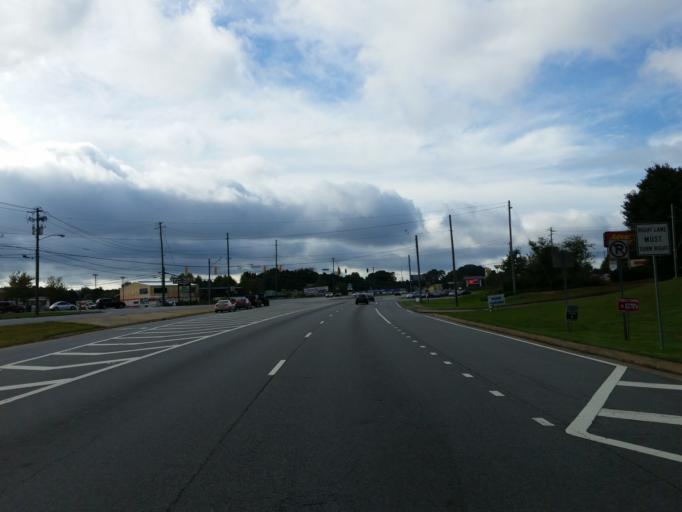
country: US
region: Georgia
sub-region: Cobb County
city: Kennesaw
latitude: 34.0028
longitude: -84.5991
